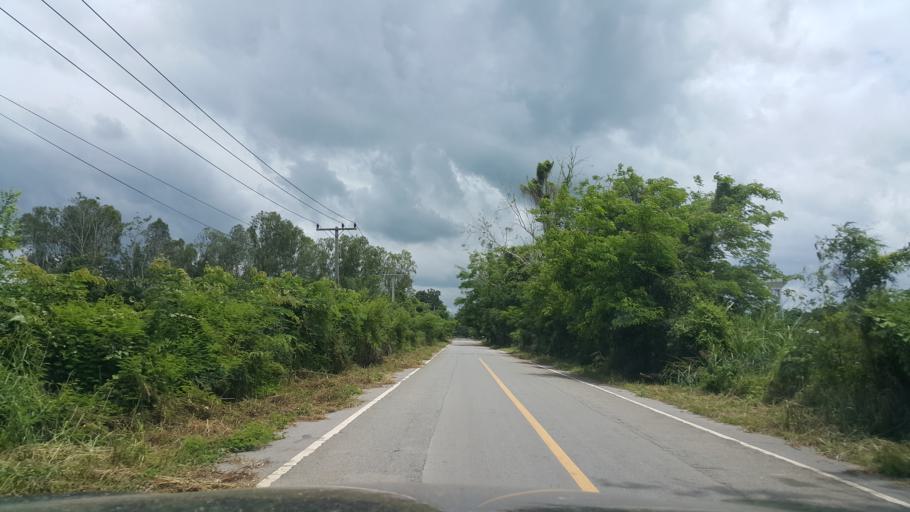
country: TH
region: Sukhothai
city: Kong Krailat
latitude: 16.9307
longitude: 99.9175
